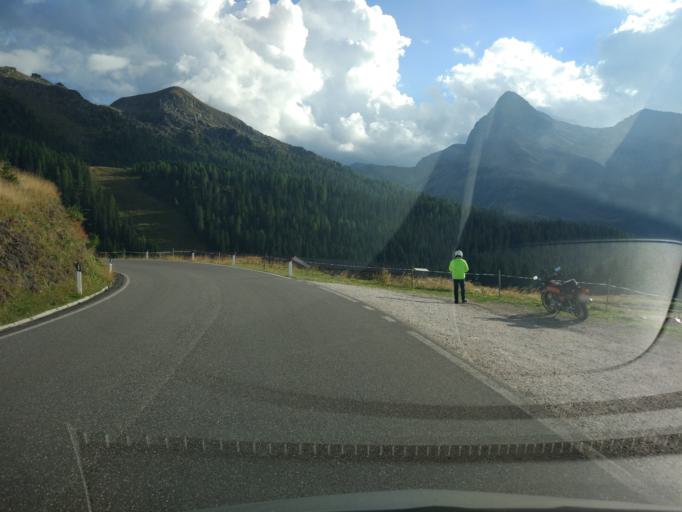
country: IT
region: Veneto
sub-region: Provincia di Belluno
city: Falcade Alto
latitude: 46.2968
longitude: 11.7795
